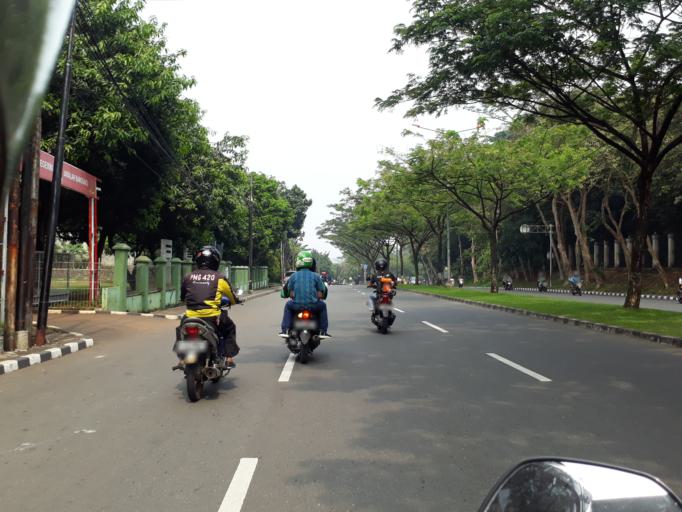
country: ID
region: West Java
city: Depok
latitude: -6.3134
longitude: 106.8606
